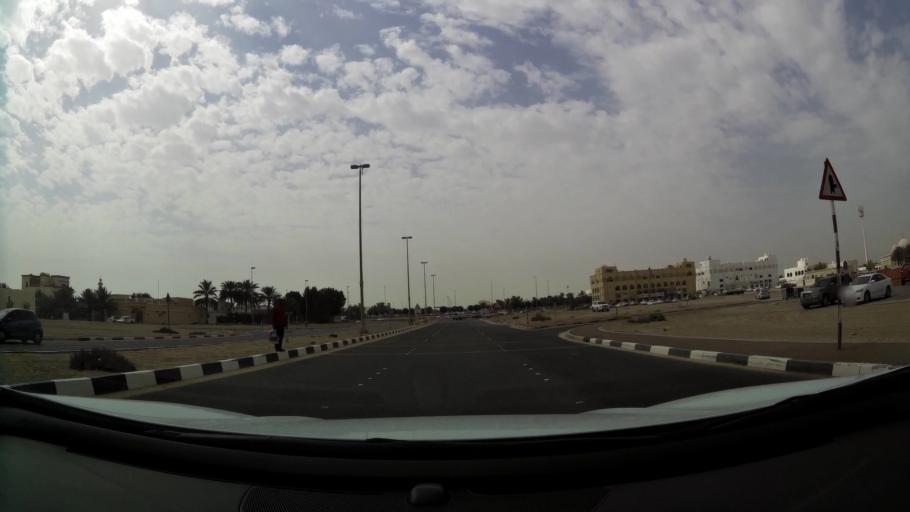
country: AE
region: Abu Dhabi
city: Abu Dhabi
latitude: 24.2975
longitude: 54.6306
